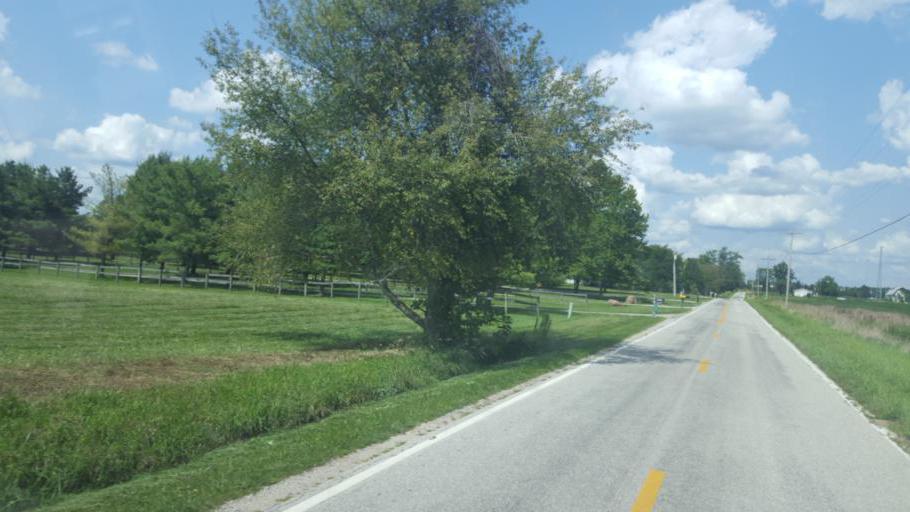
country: US
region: Ohio
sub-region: Delaware County
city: Sunbury
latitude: 40.3317
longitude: -82.8803
